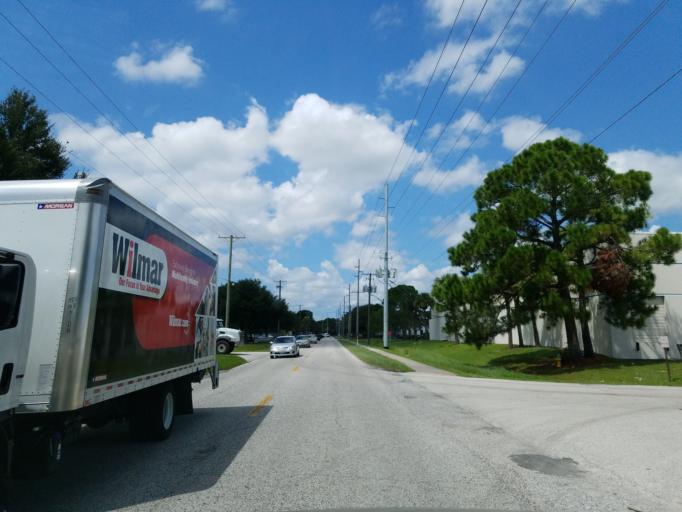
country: US
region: Florida
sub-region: Hillsborough County
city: Palm River-Clair Mel
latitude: 27.9412
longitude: -82.3459
